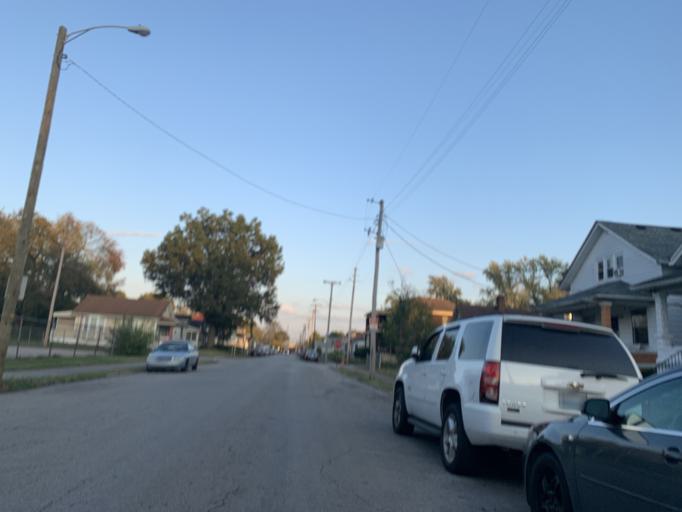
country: US
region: Indiana
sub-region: Floyd County
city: New Albany
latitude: 38.2558
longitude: -85.8097
